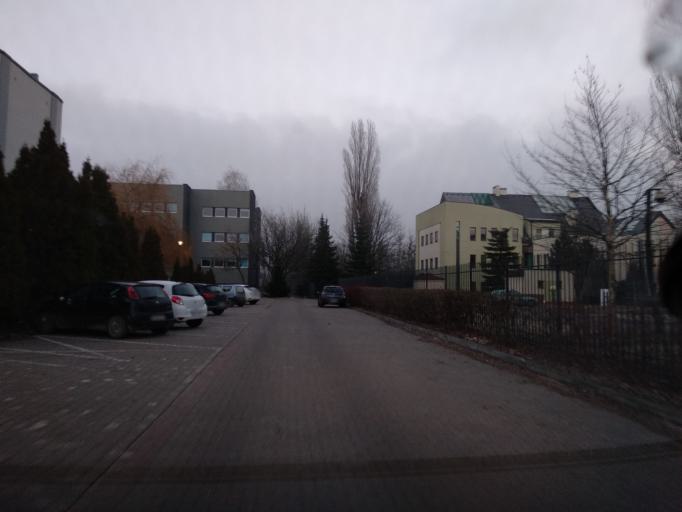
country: PL
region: Lower Silesian Voivodeship
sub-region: Powiat wroclawski
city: Wroclaw
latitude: 51.1129
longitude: 16.9821
